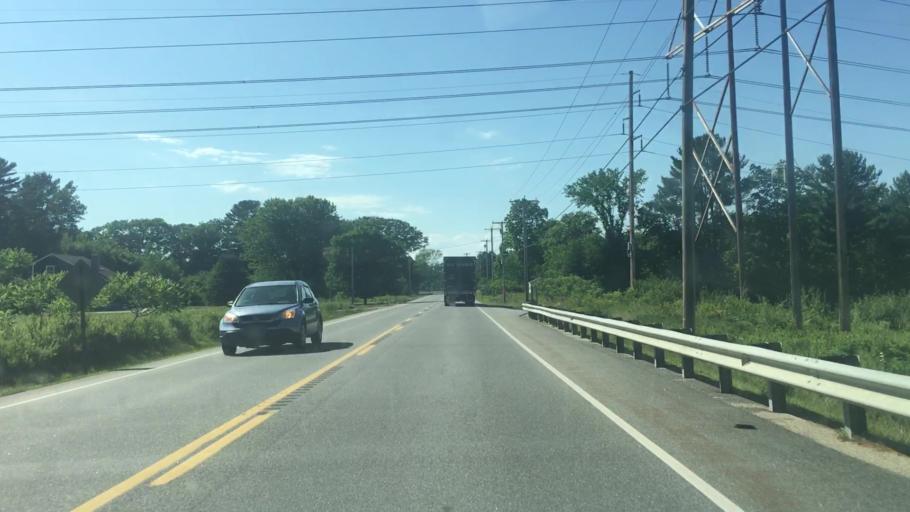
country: US
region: Maine
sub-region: York County
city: Buxton
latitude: 43.5654
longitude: -70.5017
